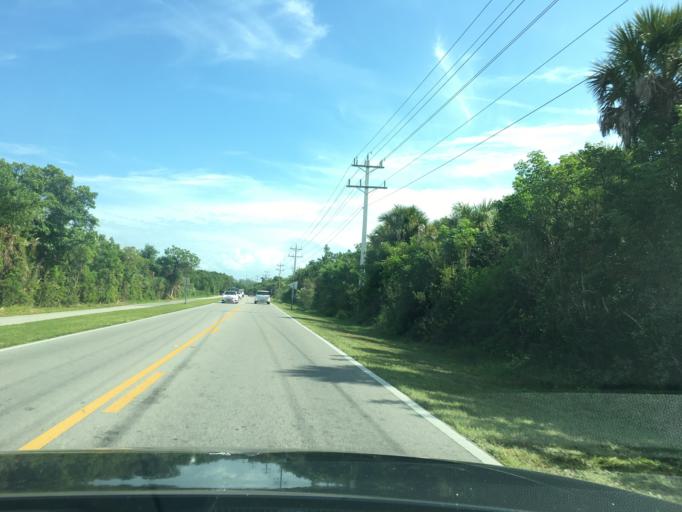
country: US
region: Florida
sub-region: Lee County
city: Saint James City
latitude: 26.4384
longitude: -82.0862
